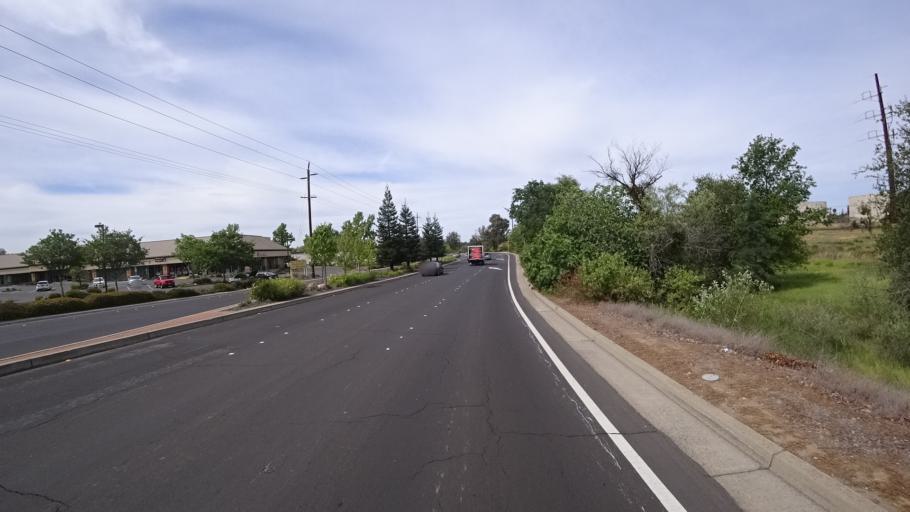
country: US
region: California
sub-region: Placer County
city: Rocklin
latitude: 38.7810
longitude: -121.2428
